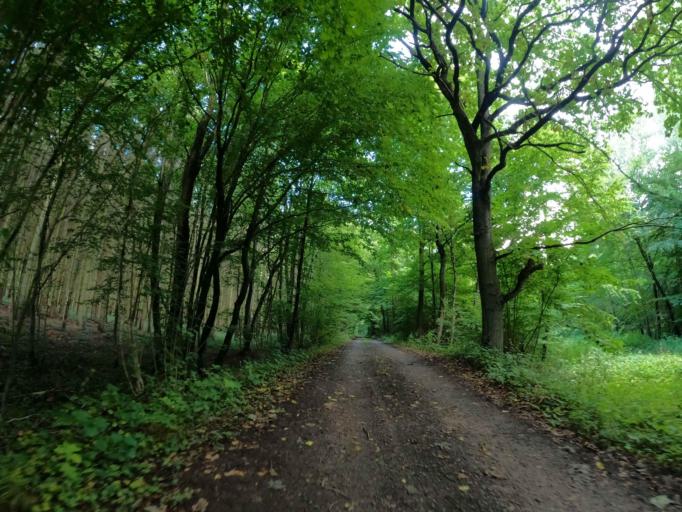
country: DE
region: Mecklenburg-Vorpommern
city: Sehlen
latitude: 54.3558
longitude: 13.4110
